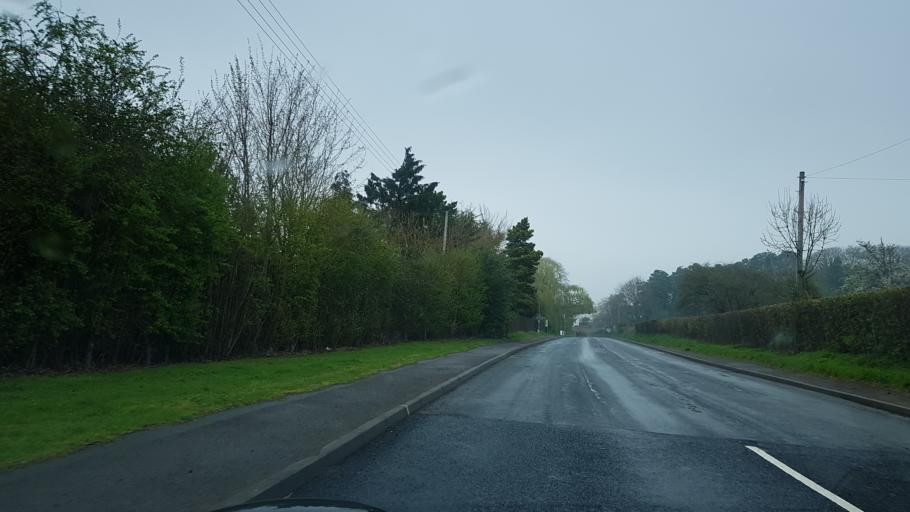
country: GB
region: England
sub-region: Herefordshire
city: Ledbury
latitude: 52.0471
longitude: -2.4271
